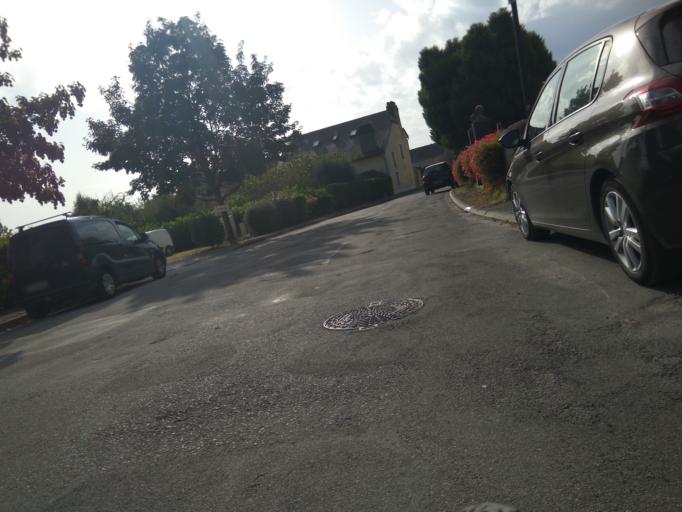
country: FR
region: Aquitaine
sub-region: Departement des Pyrenees-Atlantiques
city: Mazeres-Lezons
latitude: 43.2689
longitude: -0.3433
